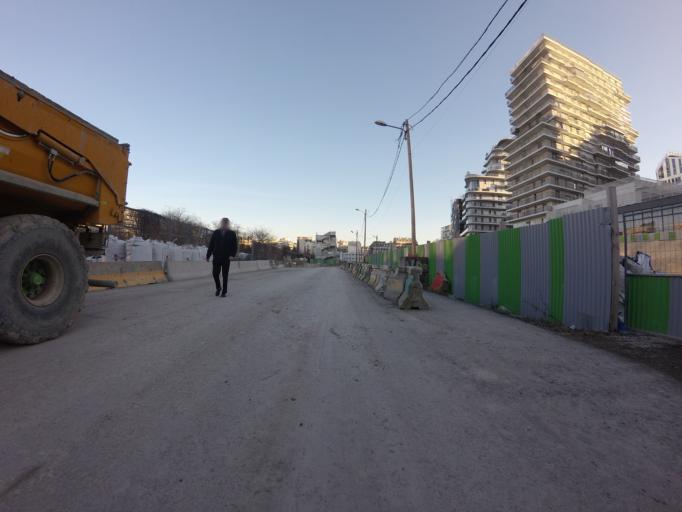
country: FR
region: Ile-de-France
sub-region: Departement des Hauts-de-Seine
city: Clichy
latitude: 48.8908
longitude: 2.3133
